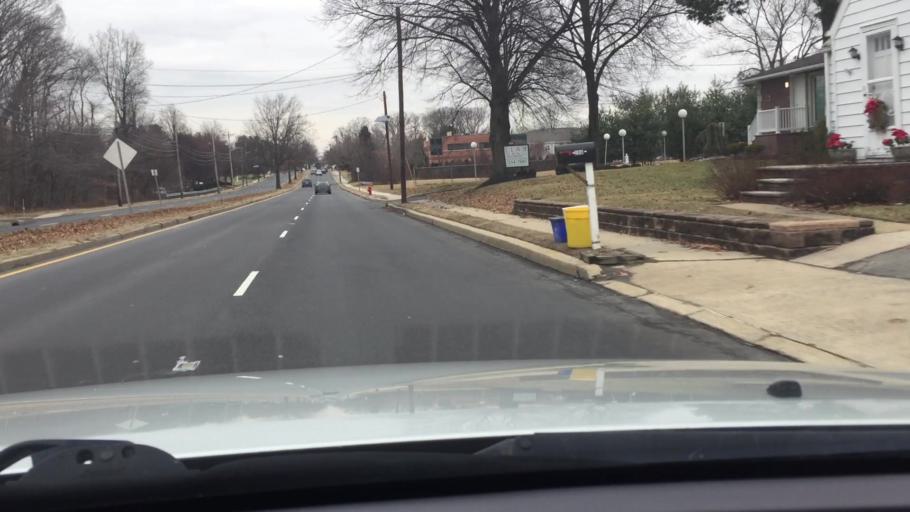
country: US
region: New Jersey
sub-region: Middlesex County
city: South River
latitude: 40.4218
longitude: -74.3895
